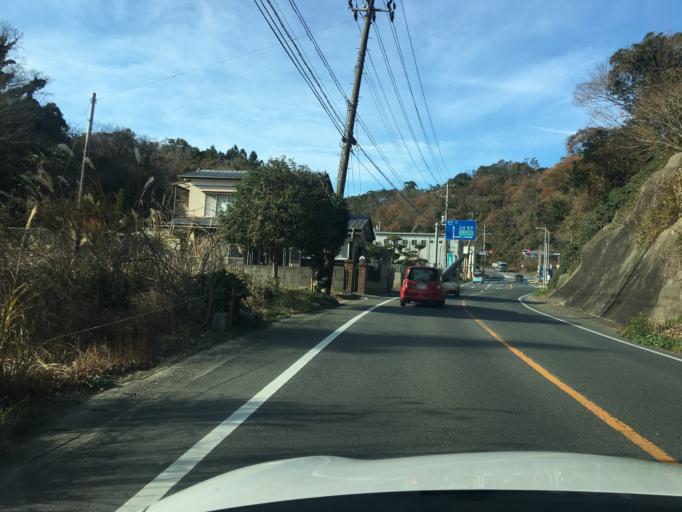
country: JP
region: Fukushima
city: Iwaki
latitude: 36.9760
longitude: 140.9535
